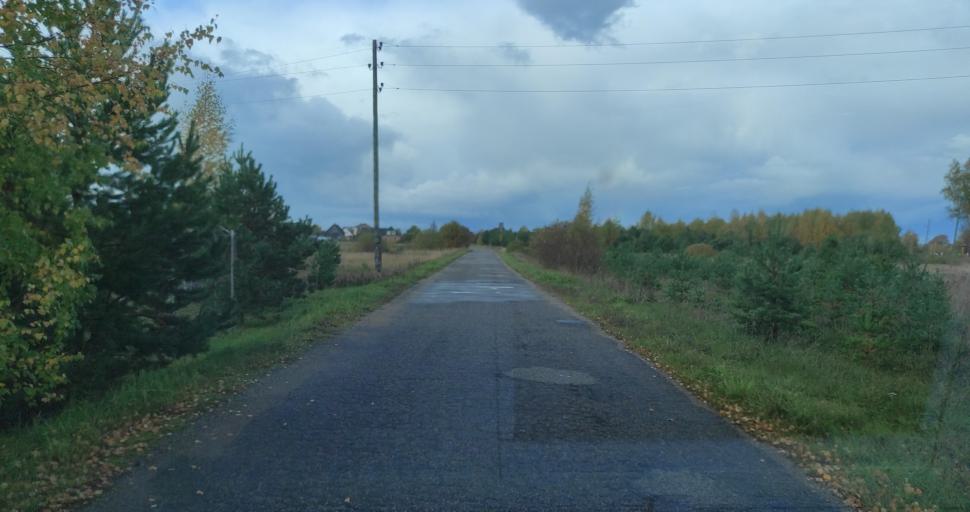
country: LV
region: Skrunda
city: Skrunda
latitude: 56.6849
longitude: 22.0584
